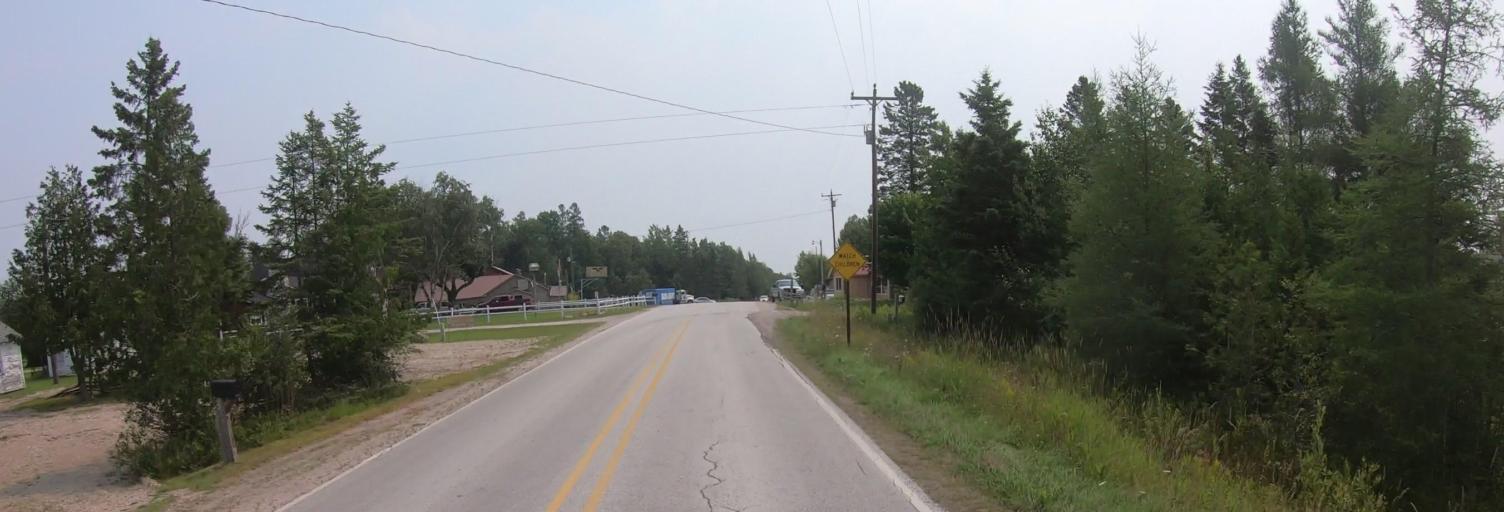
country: CA
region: Ontario
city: Thessalon
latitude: 45.9766
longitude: -83.6644
